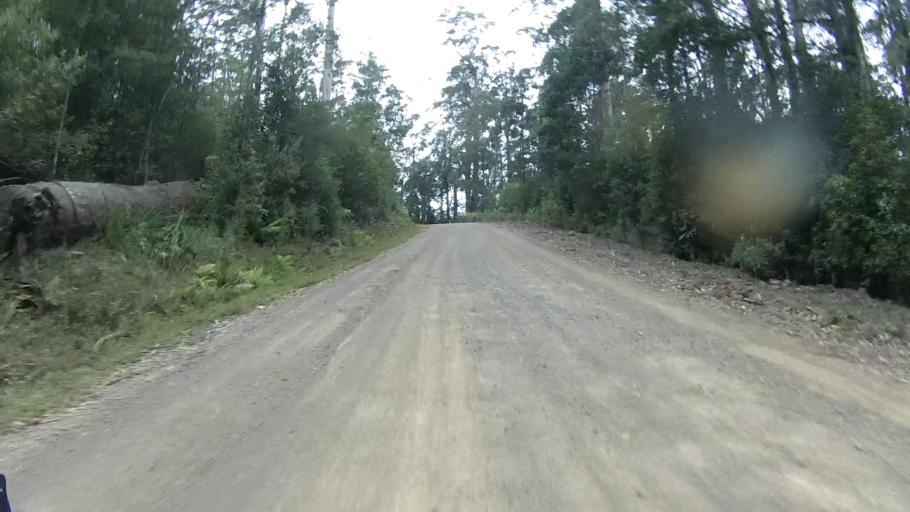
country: AU
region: Tasmania
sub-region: Sorell
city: Sorell
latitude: -42.7006
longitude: 147.8551
